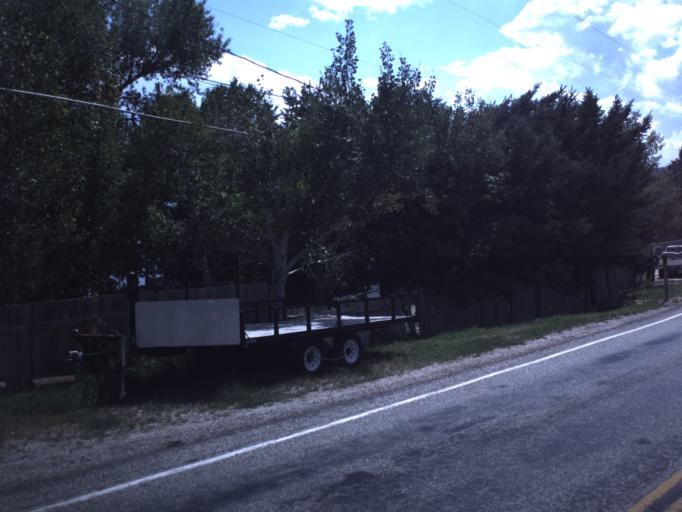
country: US
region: Idaho
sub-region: Bear Lake County
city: Paris
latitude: 41.9943
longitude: -111.4110
